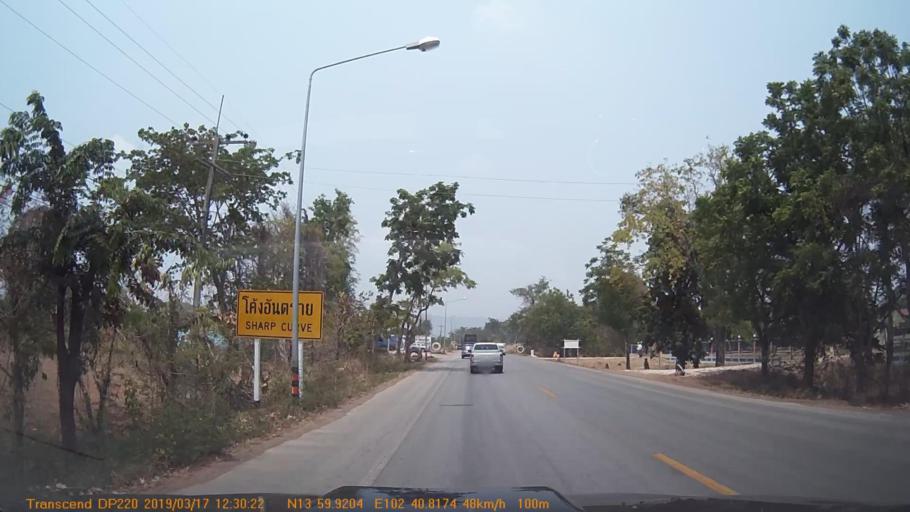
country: TH
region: Sa Kaeo
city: Ta Phraya
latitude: 13.9987
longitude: 102.6803
